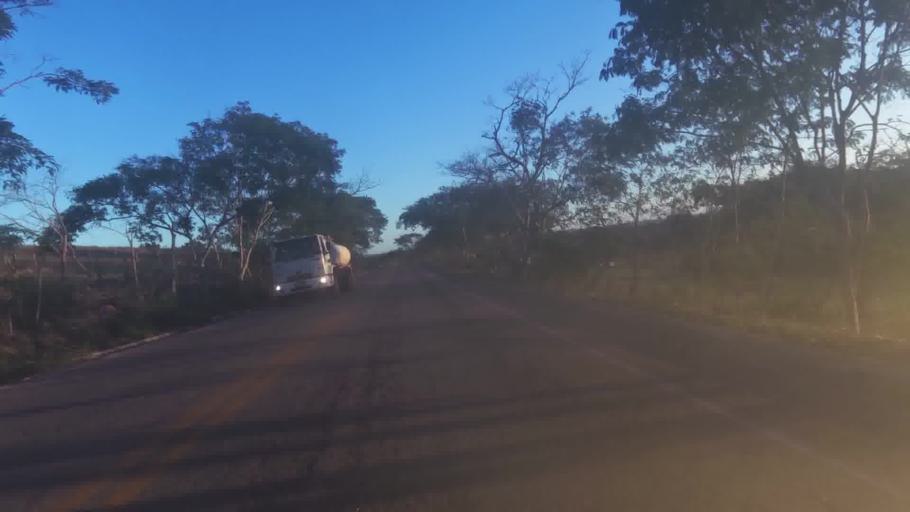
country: BR
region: Espirito Santo
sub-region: Marataizes
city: Marataizes
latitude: -21.1981
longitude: -40.9688
